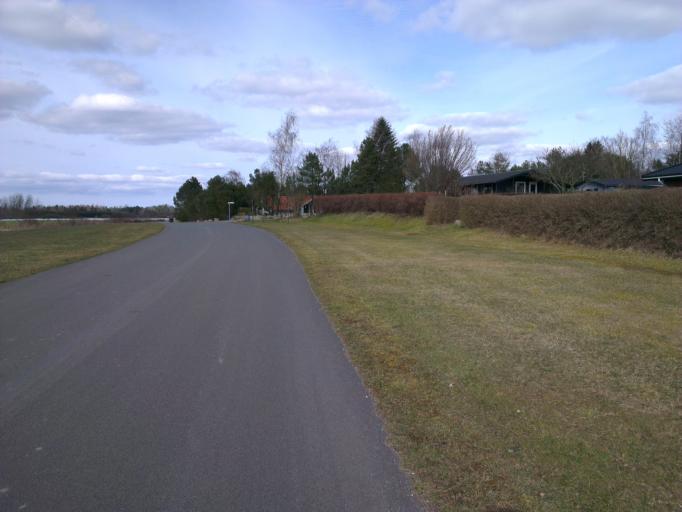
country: DK
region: Zealand
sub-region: Roskilde Kommune
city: Jyllinge
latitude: 55.7746
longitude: 12.0521
